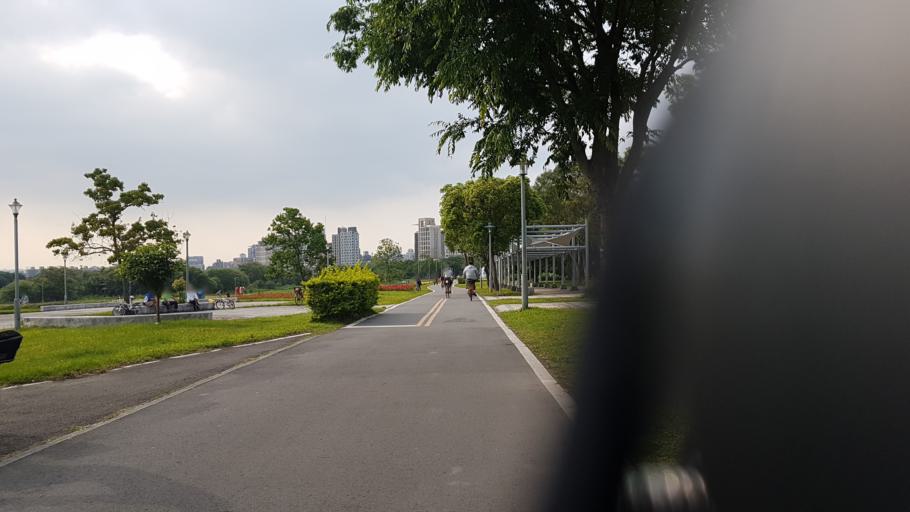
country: TW
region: Taipei
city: Taipei
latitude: 25.0155
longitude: 121.5255
